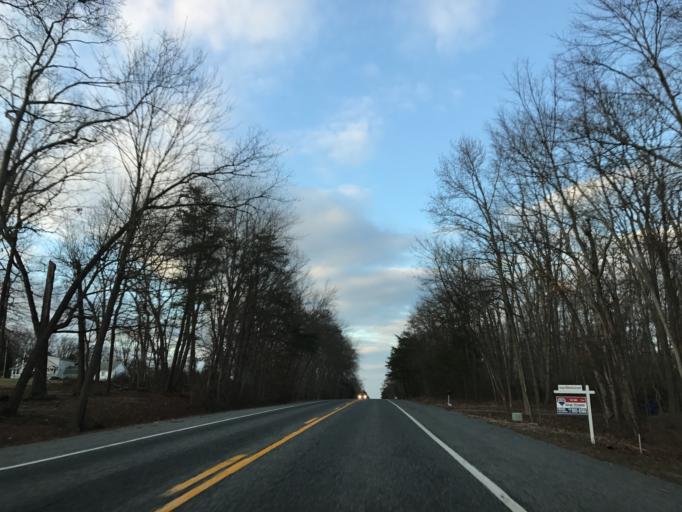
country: US
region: Maryland
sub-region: Cecil County
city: Charlestown
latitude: 39.5245
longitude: -75.9539
